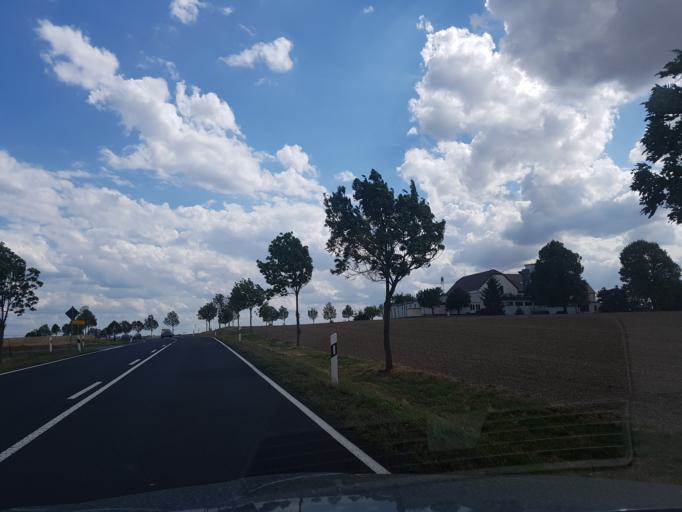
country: DE
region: Saxony
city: Priestewitz
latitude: 51.2418
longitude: 13.5493
